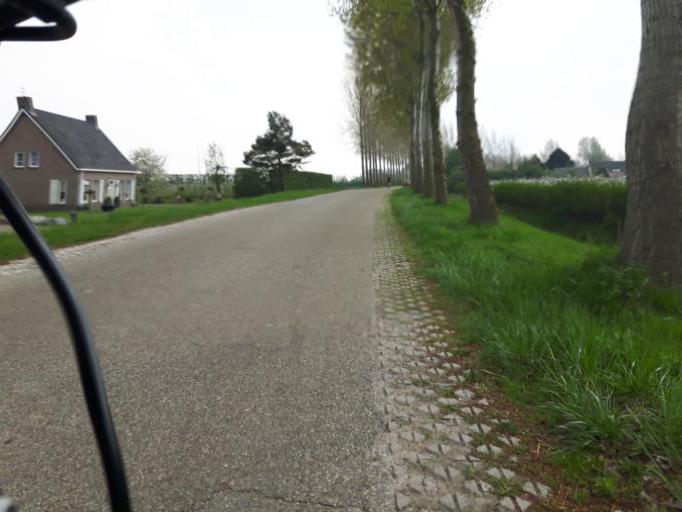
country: NL
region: Zeeland
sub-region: Gemeente Borsele
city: Borssele
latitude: 51.4571
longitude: 3.8064
